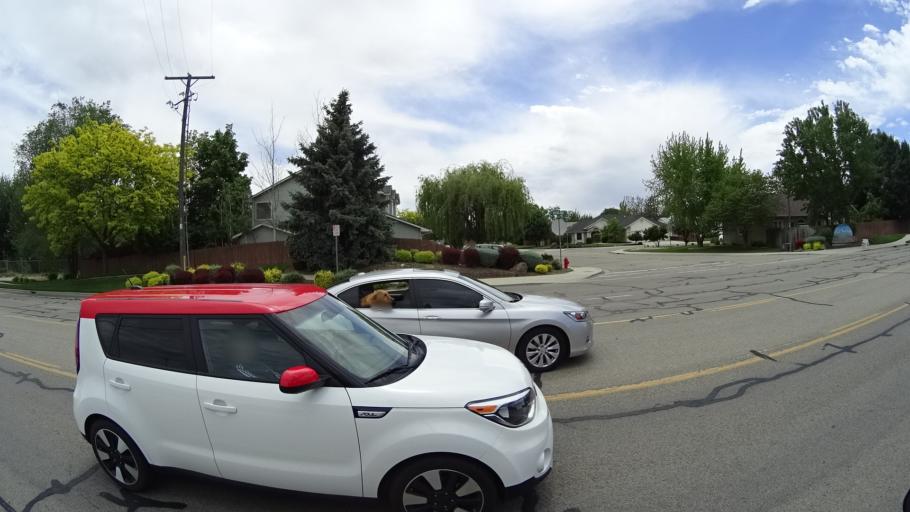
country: US
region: Idaho
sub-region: Ada County
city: Meridian
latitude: 43.5903
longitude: -116.3772
